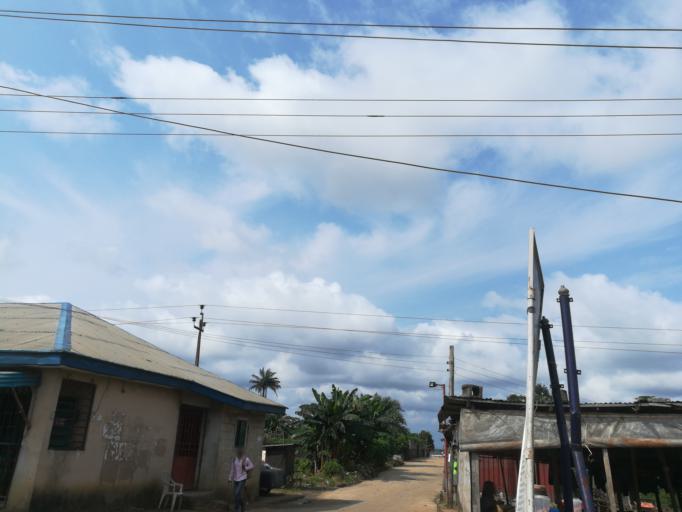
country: NG
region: Rivers
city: Okrika
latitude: 4.7607
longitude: 7.0971
